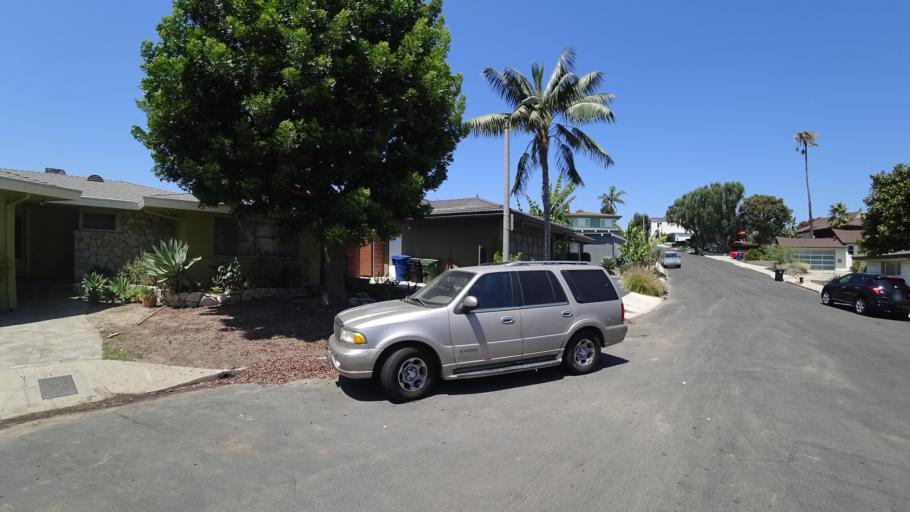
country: US
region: California
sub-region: Los Angeles County
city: View Park-Windsor Hills
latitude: 34.0118
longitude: -118.3577
